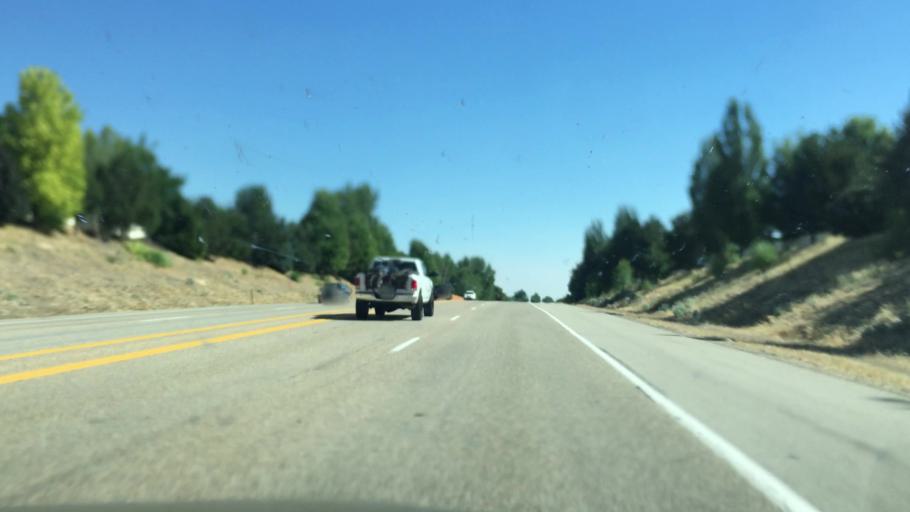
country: US
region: Idaho
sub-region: Ada County
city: Eagle
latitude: 43.7161
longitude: -116.3194
